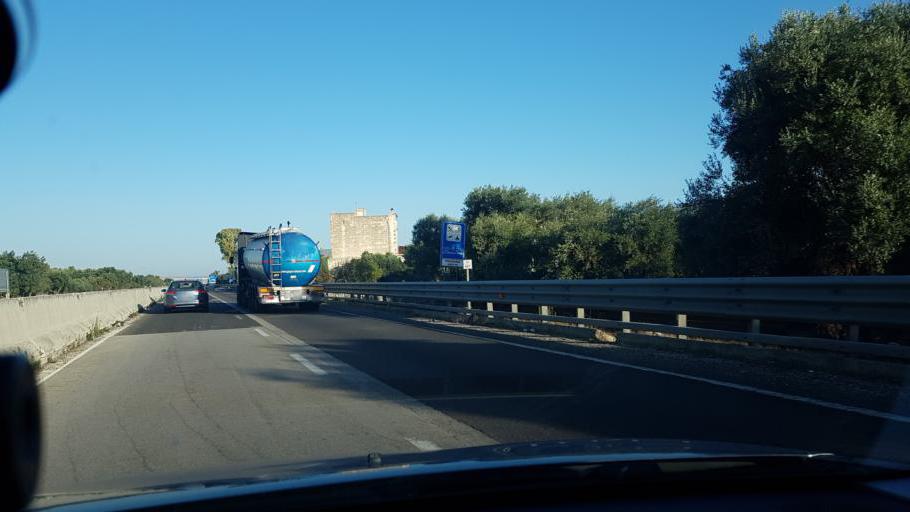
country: IT
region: Apulia
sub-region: Provincia di Brindisi
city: Fasano
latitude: 40.8454
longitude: 17.3634
